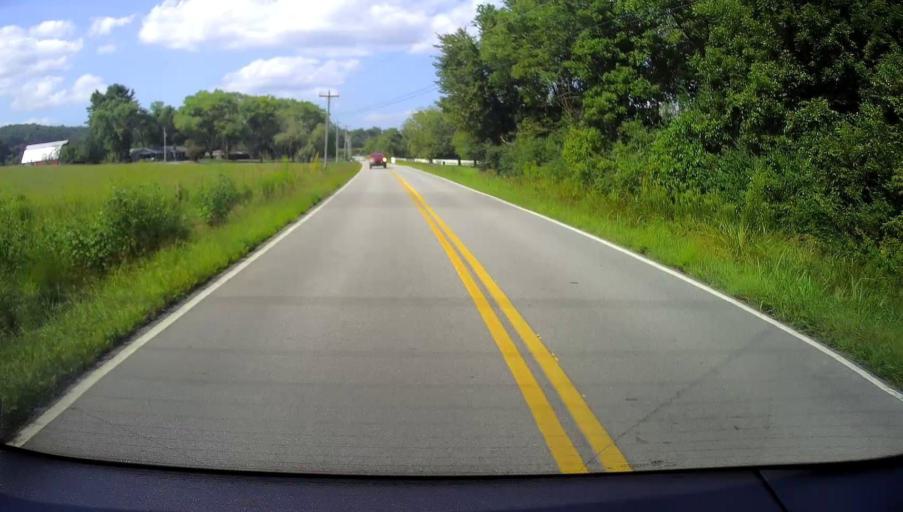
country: US
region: Tennessee
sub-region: Hamilton County
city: Apison
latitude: 34.9833
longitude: -85.0647
